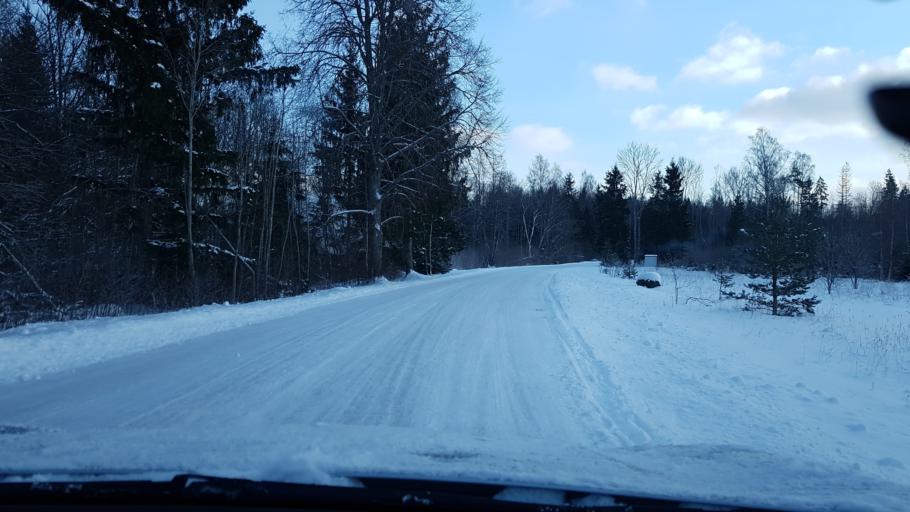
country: EE
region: Harju
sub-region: Nissi vald
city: Turba
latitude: 59.1521
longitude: 24.1485
